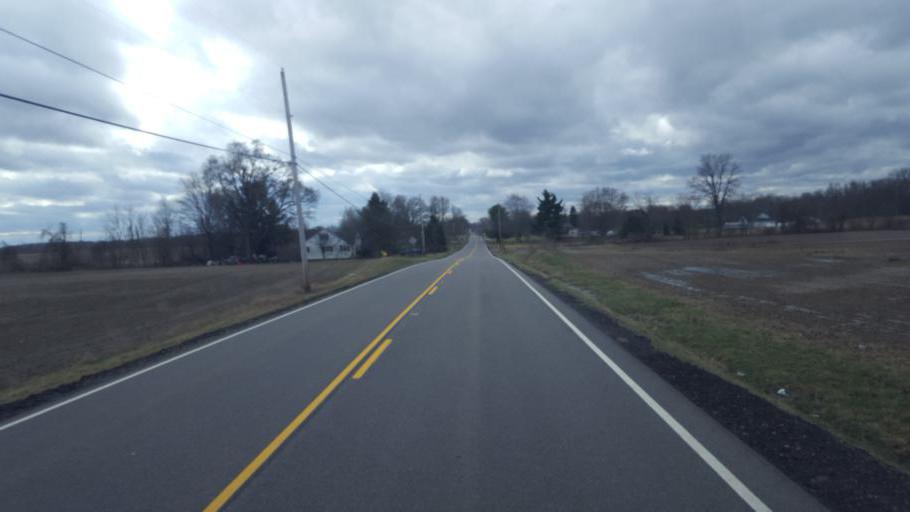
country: US
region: Ohio
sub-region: Knox County
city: Mount Vernon
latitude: 40.3224
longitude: -82.5080
